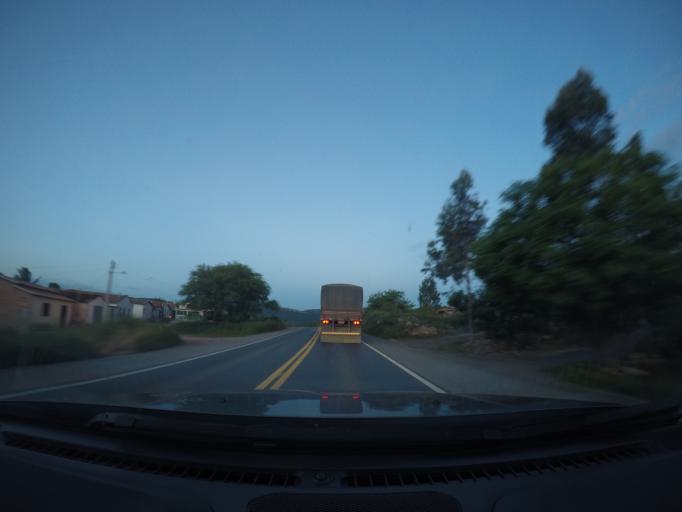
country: BR
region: Bahia
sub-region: Seabra
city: Seabra
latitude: -12.4842
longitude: -41.7220
